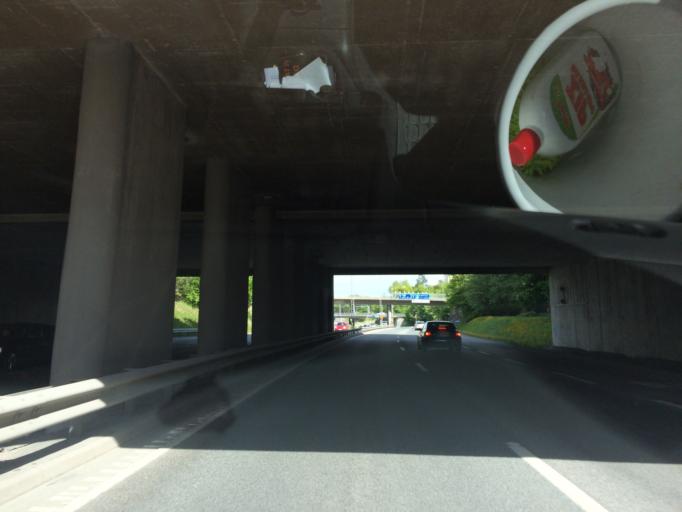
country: SE
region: Stockholm
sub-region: Norrtalje Kommun
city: Bergshamra
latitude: 59.3800
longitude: 18.0343
